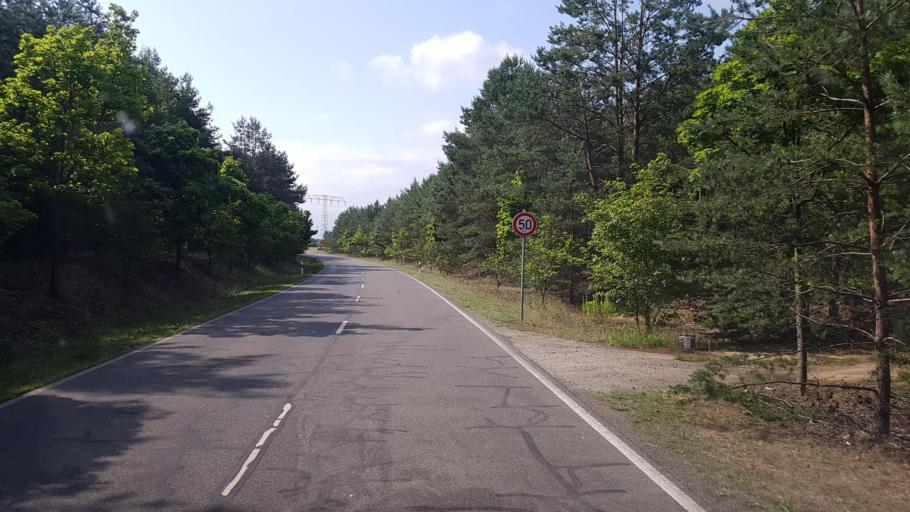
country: DE
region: Brandenburg
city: Grossraschen
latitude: 51.5900
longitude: 14.0283
